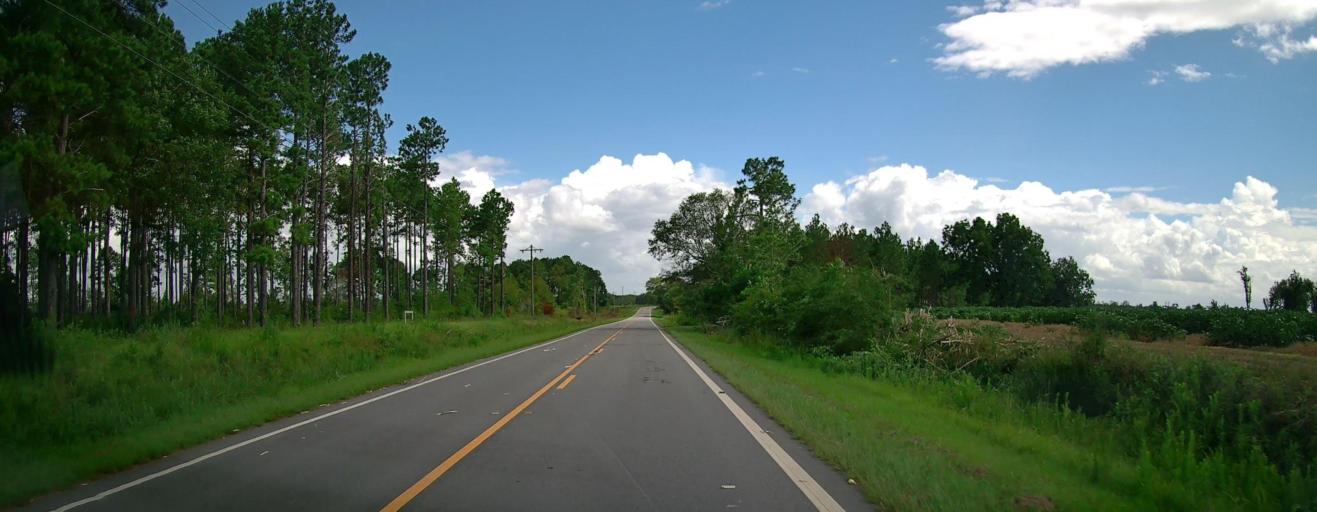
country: US
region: Georgia
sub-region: Irwin County
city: Ocilla
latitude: 31.6306
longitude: -83.1677
